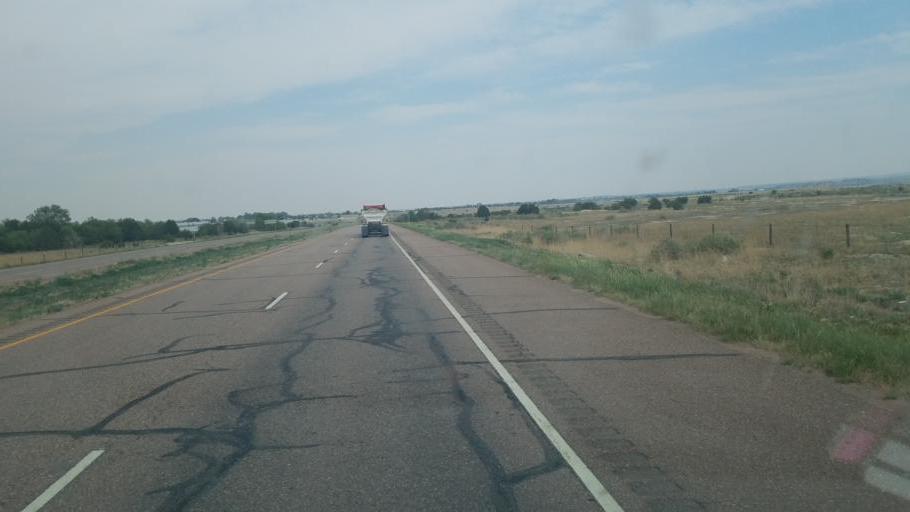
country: US
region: Colorado
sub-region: Fremont County
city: Penrose
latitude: 38.4132
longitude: -105.0220
